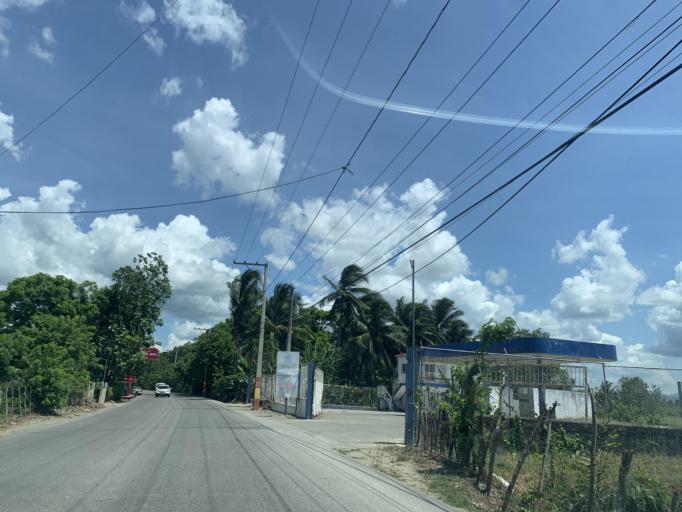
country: DO
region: Puerto Plata
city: Cabarete
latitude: 19.6919
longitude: -70.3804
